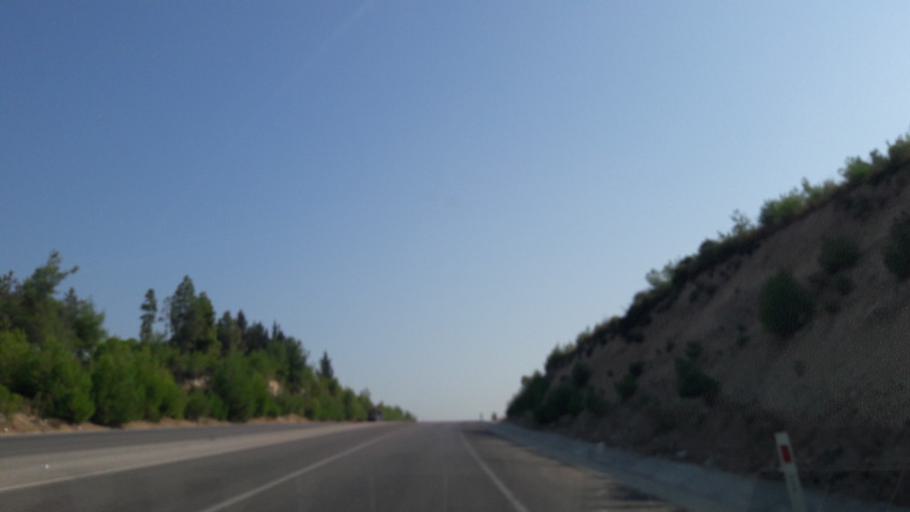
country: TR
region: Adana
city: Sagkaya
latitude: 37.1530
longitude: 35.5459
